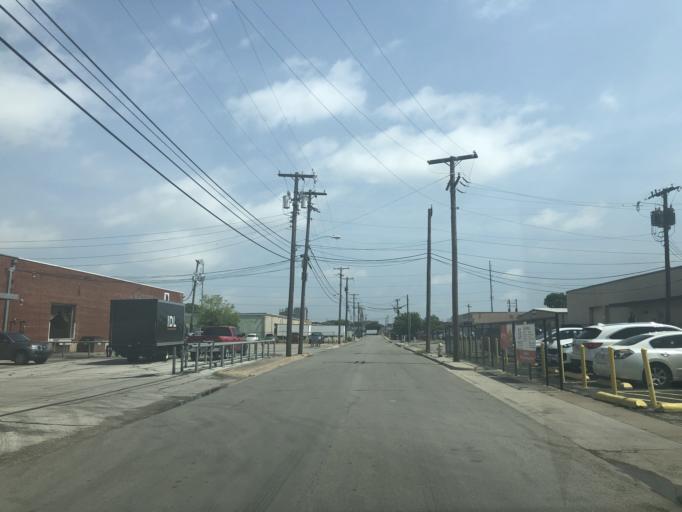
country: US
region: Texas
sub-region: Dallas County
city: Dallas
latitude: 32.8040
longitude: -96.8651
